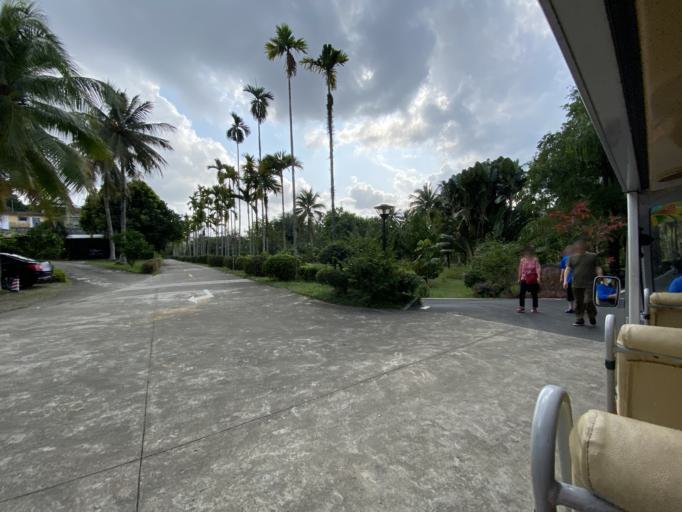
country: CN
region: Hainan
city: Nanqiao
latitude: 18.7344
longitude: 110.1935
